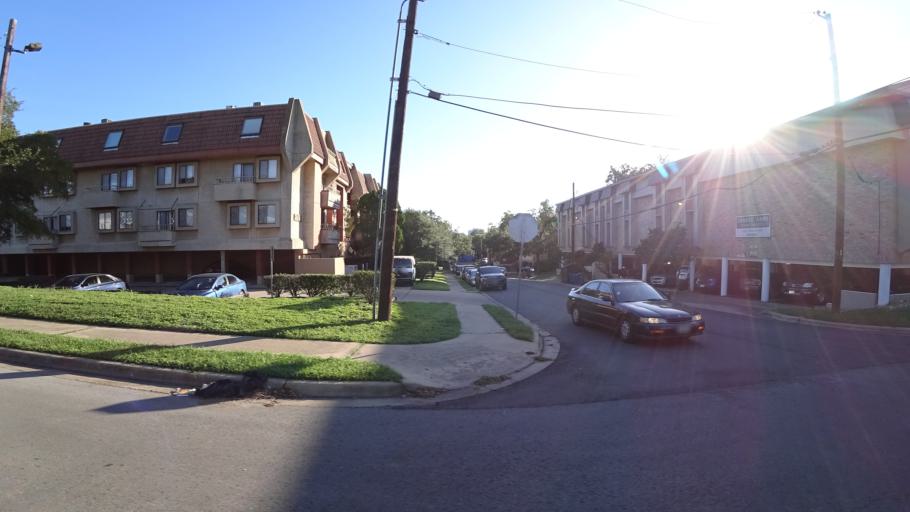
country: US
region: Texas
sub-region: Travis County
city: Austin
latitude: 30.2960
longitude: -97.7356
